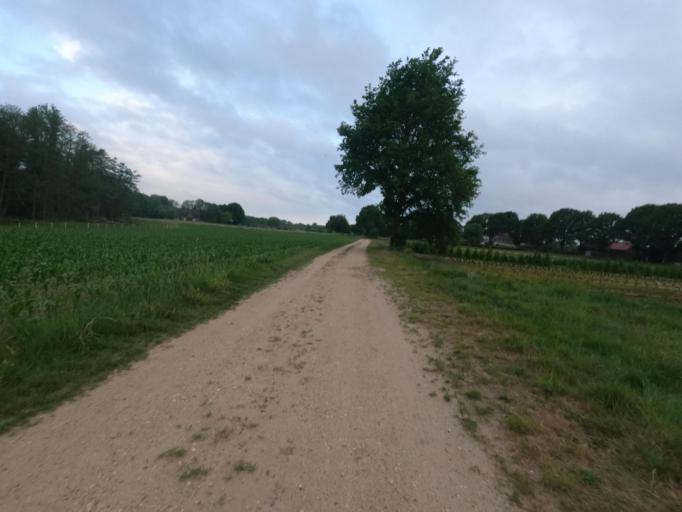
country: NL
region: Limburg
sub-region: Gemeente Roerdalen
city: Vlodrop
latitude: 51.1371
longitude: 6.1016
